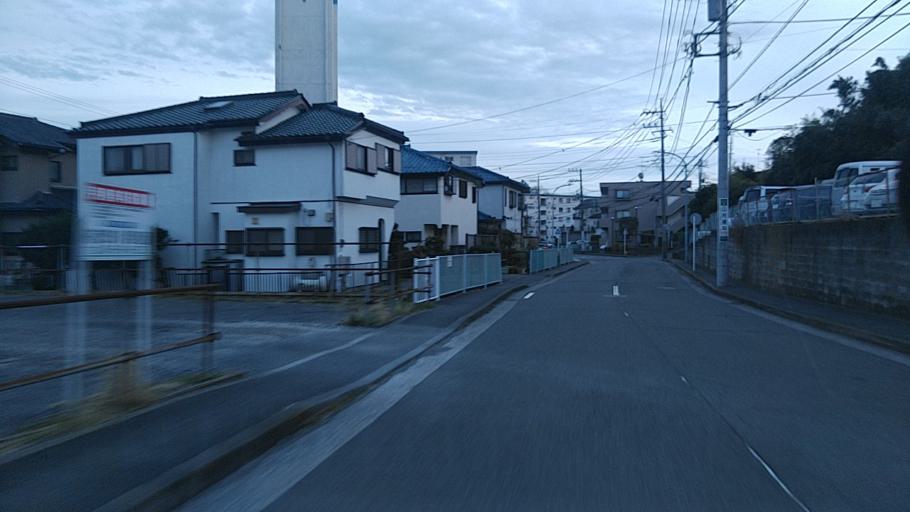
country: JP
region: Kanagawa
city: Fujisawa
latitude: 35.4143
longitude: 139.4921
